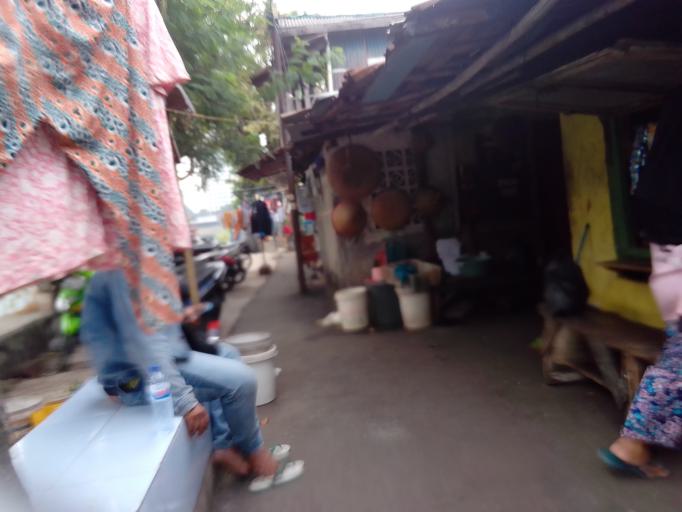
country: ID
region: Jakarta Raya
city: Jakarta
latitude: -6.1996
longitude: 106.8184
